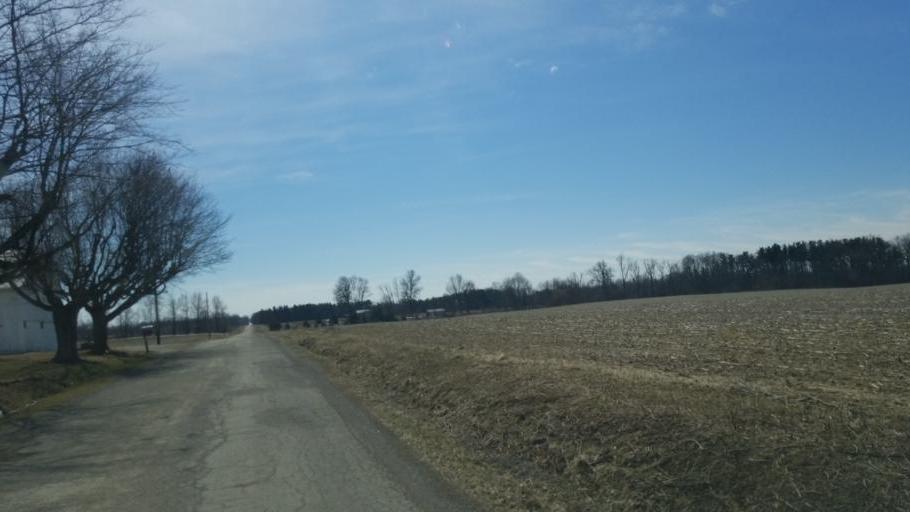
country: US
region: Ohio
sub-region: Crawford County
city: Galion
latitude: 40.7007
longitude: -82.7462
